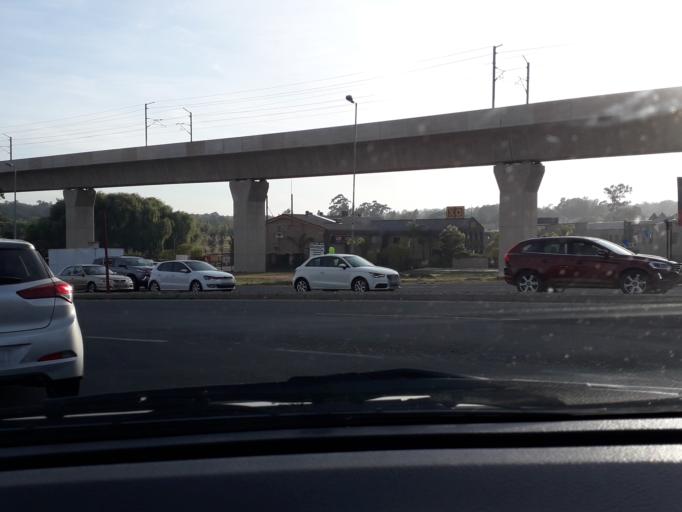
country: ZA
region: Gauteng
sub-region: City of Johannesburg Metropolitan Municipality
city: Midrand
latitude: -25.9560
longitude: 28.1403
